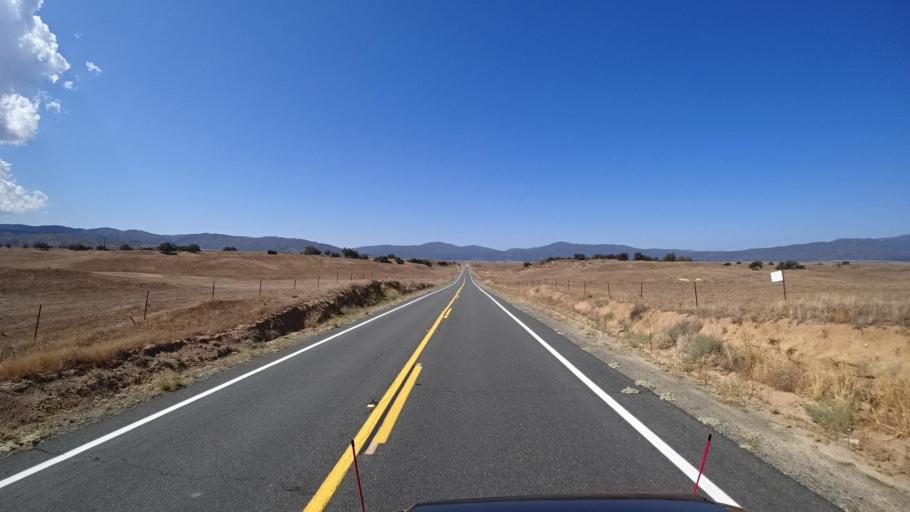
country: US
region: California
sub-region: San Diego County
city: Julian
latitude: 33.2620
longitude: -116.6620
